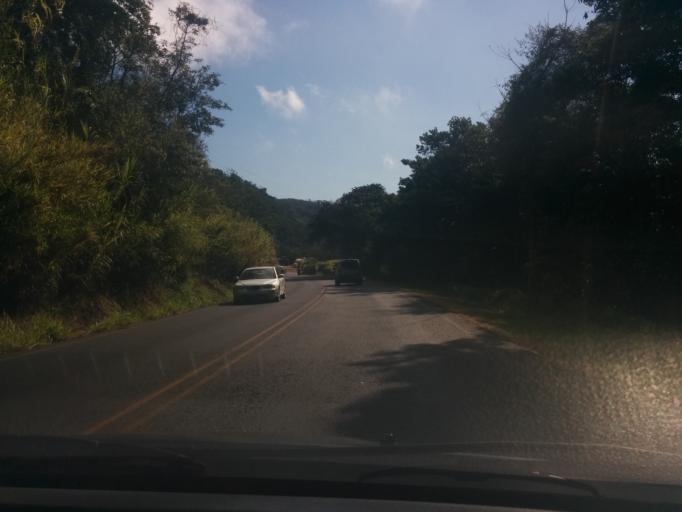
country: CR
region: Alajuela
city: San Rafael
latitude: 10.0690
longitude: -84.4947
